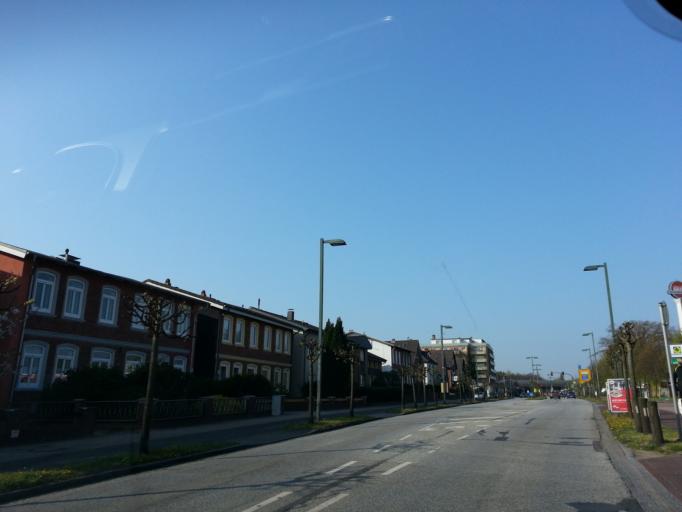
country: DE
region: Schleswig-Holstein
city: Bad Schwartau
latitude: 53.9047
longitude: 10.6902
